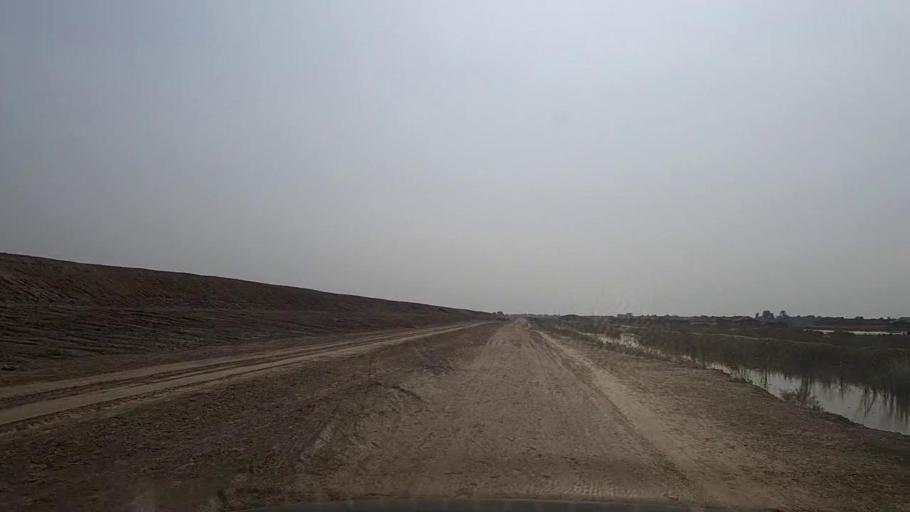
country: PK
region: Sindh
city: Thatta
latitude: 24.5698
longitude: 67.9133
